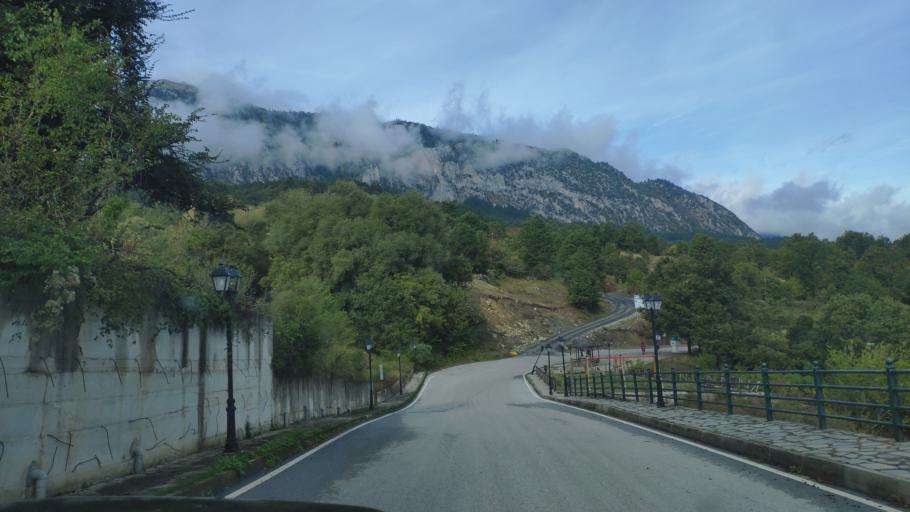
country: GR
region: West Macedonia
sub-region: Nomos Kastorias
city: Nestorio
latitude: 40.2760
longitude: 20.9749
